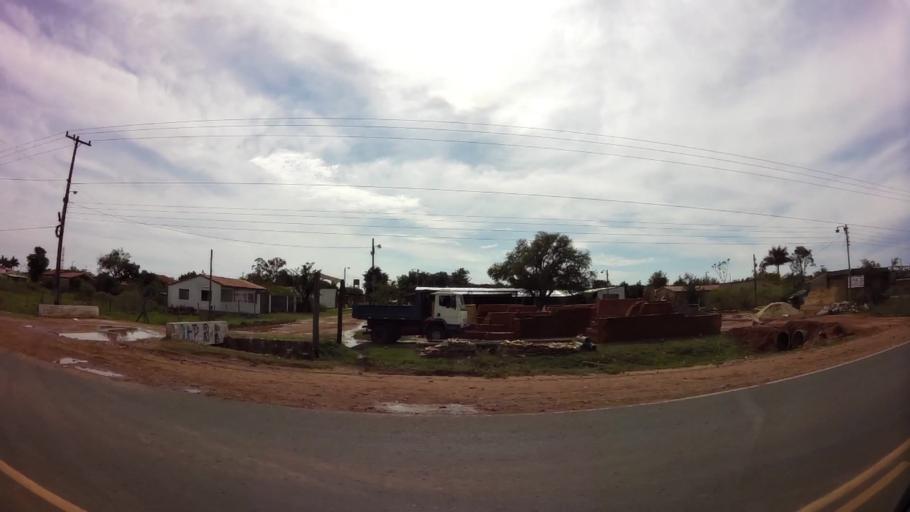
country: PY
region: Central
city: Limpio
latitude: -25.1309
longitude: -57.4807
